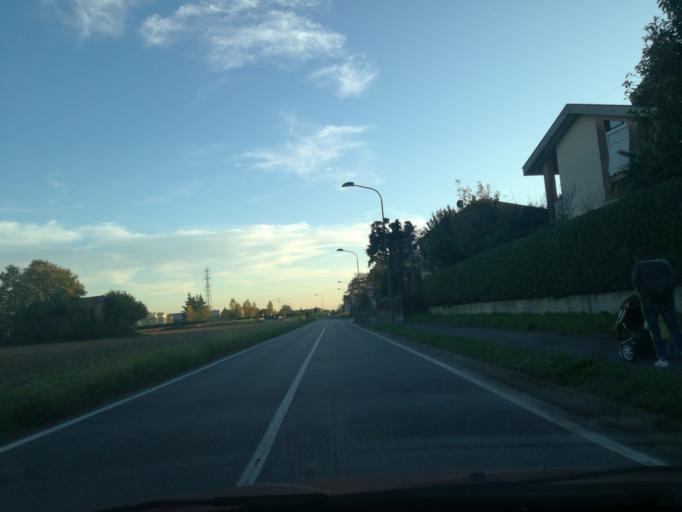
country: IT
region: Lombardy
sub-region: Provincia di Monza e Brianza
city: Burago di Molgora
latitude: 45.6085
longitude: 9.3807
